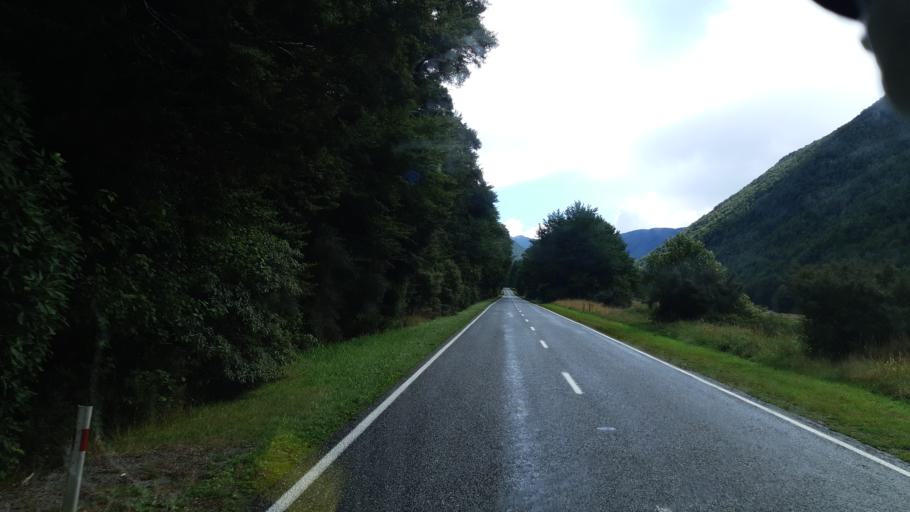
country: NZ
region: Canterbury
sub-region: Hurunui District
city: Amberley
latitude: -42.3806
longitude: 172.3210
